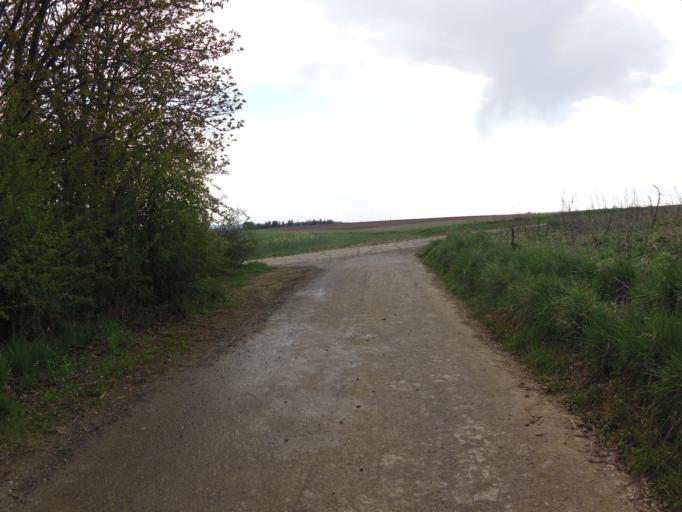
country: DE
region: Bavaria
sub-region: Regierungsbezirk Unterfranken
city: Rimpar
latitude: 49.8663
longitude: 9.9550
